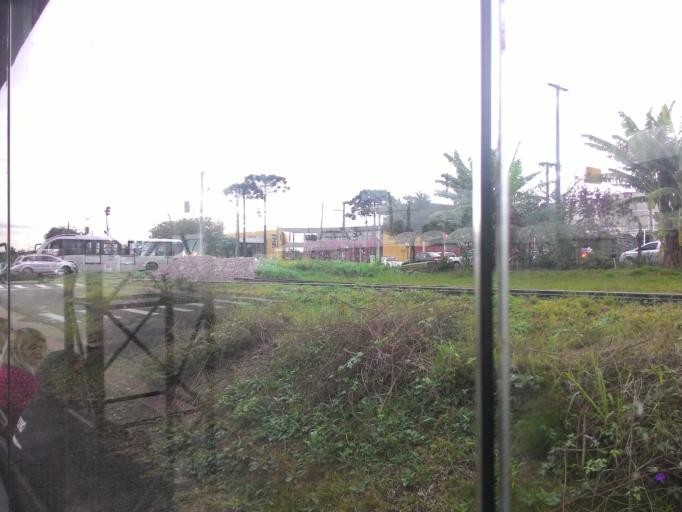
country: BR
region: Parana
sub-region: Pinhais
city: Pinhais
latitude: -25.4402
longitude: -49.2213
